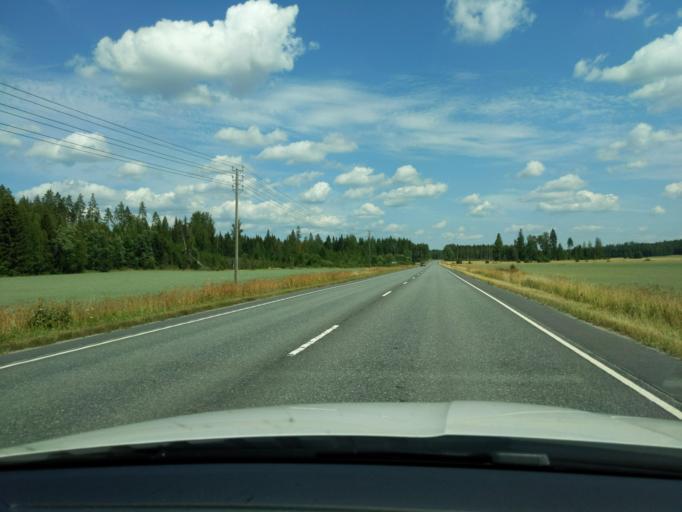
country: FI
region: Uusimaa
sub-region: Helsinki
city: Maentsaelae
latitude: 60.5713
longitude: 25.2186
